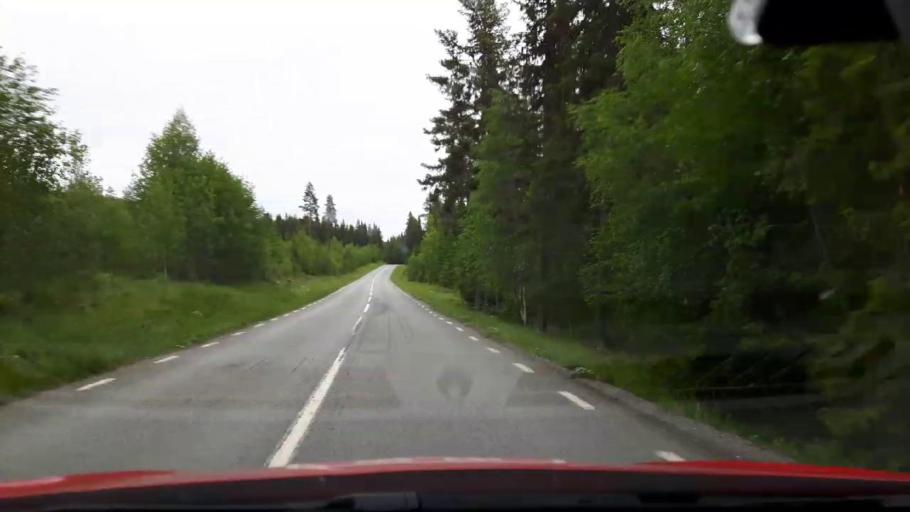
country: SE
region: Jaemtland
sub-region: Stroemsunds Kommun
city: Stroemsund
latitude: 63.4476
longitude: 15.4719
